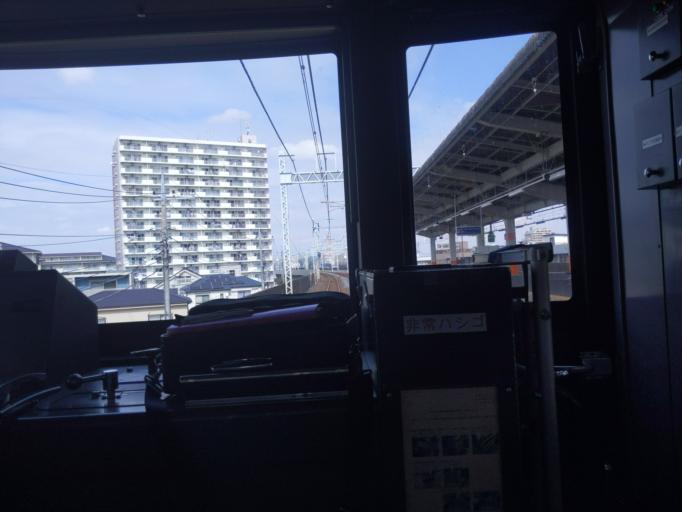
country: JP
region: Saitama
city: Soka
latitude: 35.8148
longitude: 139.8013
